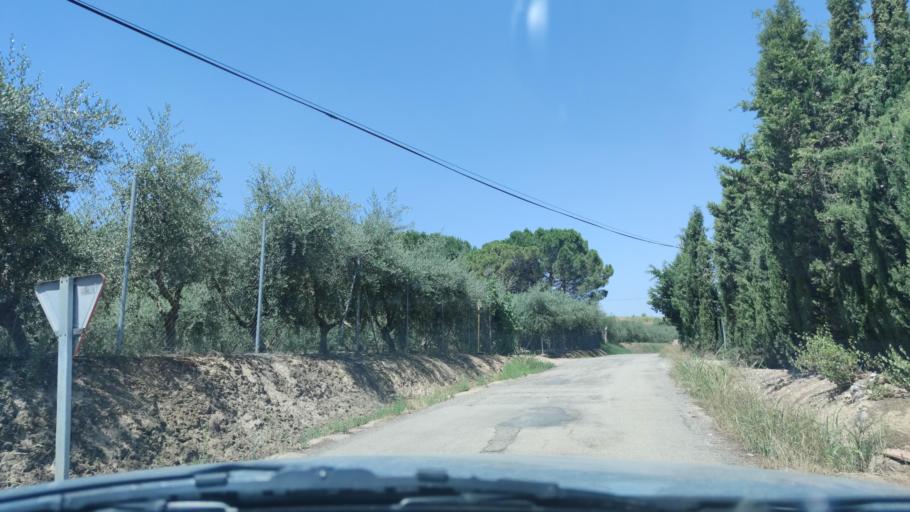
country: ES
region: Catalonia
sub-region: Provincia de Lleida
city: Torrefarrera
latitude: 41.6532
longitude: 0.5860
